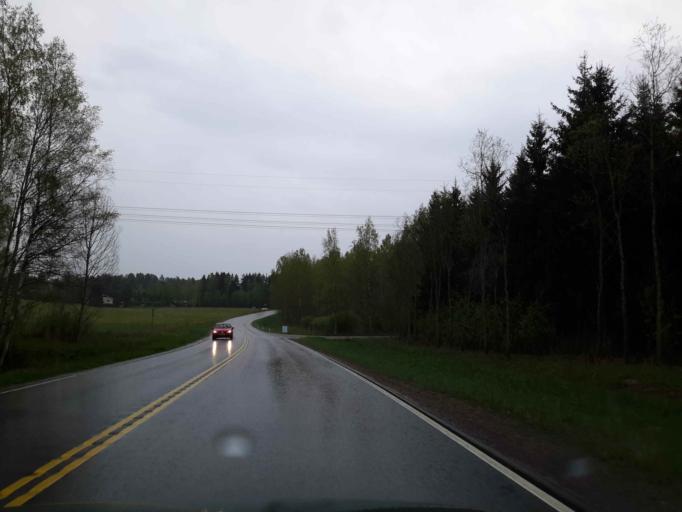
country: FI
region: Uusimaa
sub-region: Helsinki
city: Vihti
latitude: 60.3831
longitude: 24.5148
